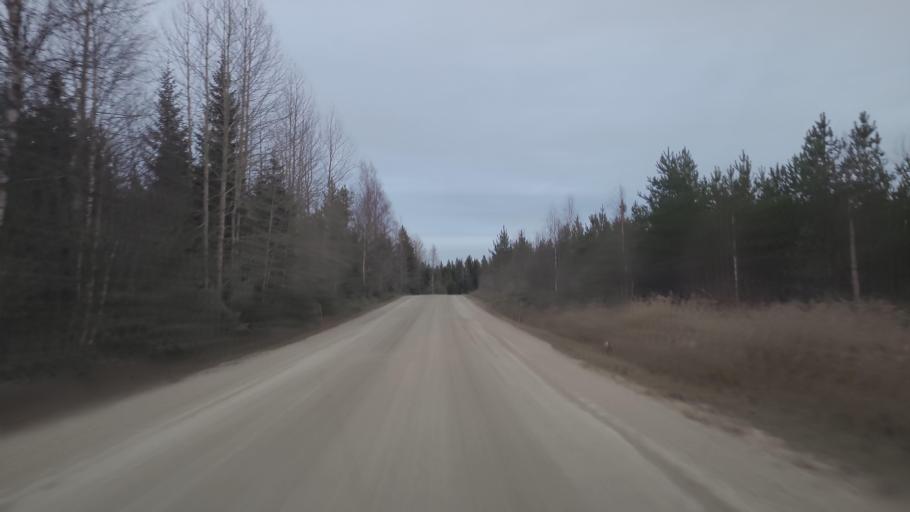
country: FI
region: Lapland
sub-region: Kemi-Tornio
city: Tervola
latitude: 66.0709
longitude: 24.8825
